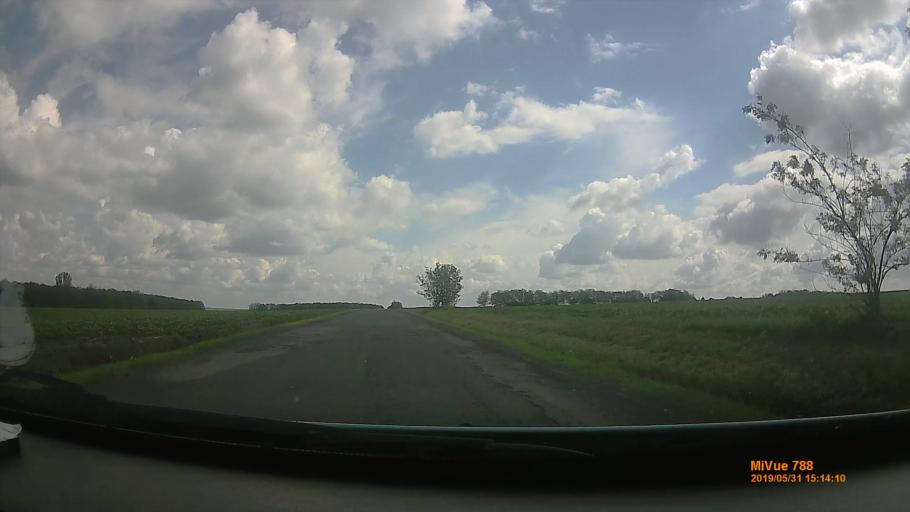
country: HU
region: Borsod-Abauj-Zemplen
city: Tiszaluc
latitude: 48.0991
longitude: 21.0629
